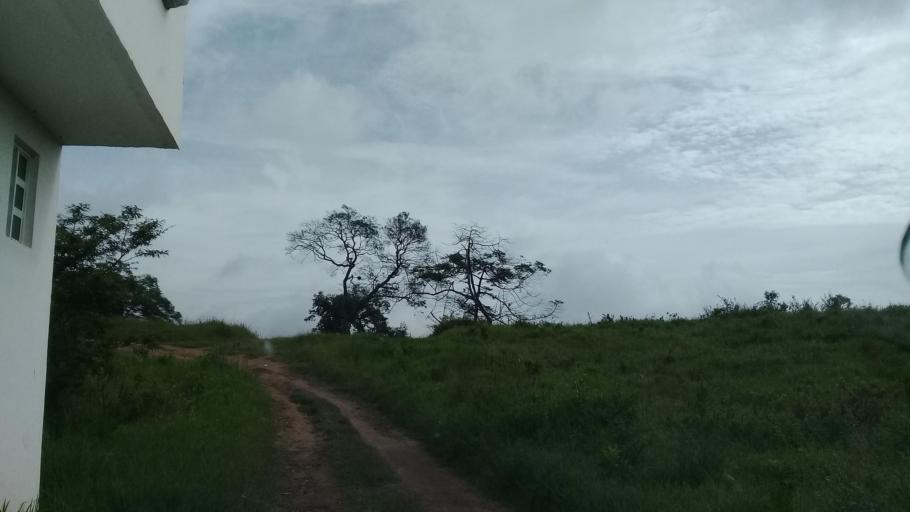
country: MX
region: Veracruz
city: El Castillo
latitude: 19.5543
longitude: -96.8789
